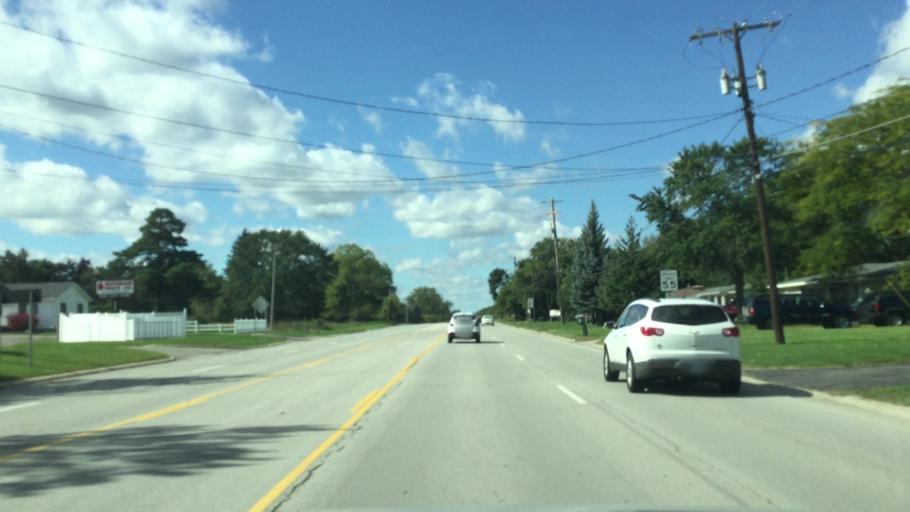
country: US
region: Michigan
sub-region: Genesee County
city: Flint
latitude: 42.9439
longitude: -83.7333
